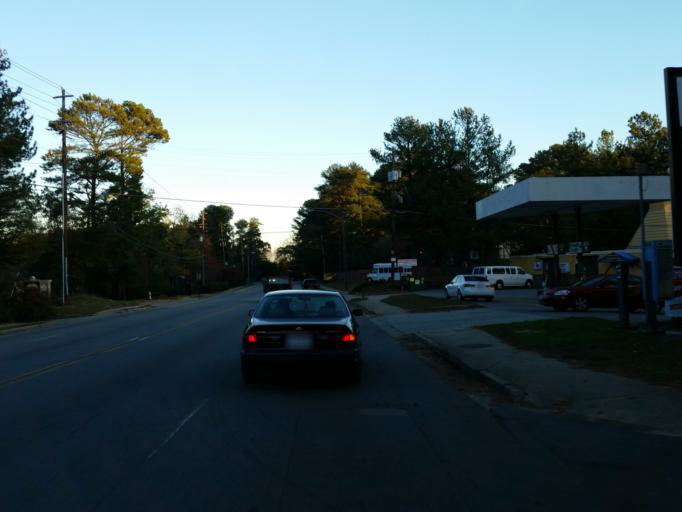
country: US
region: Georgia
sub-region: Cobb County
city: Fair Oaks
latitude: 33.9330
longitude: -84.5012
